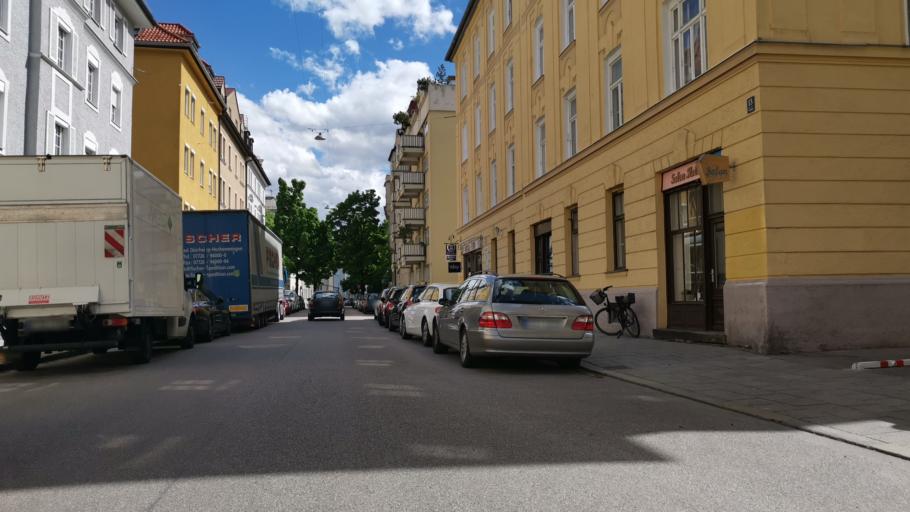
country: DE
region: Bavaria
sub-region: Upper Bavaria
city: Munich
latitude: 48.1508
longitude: 11.5347
